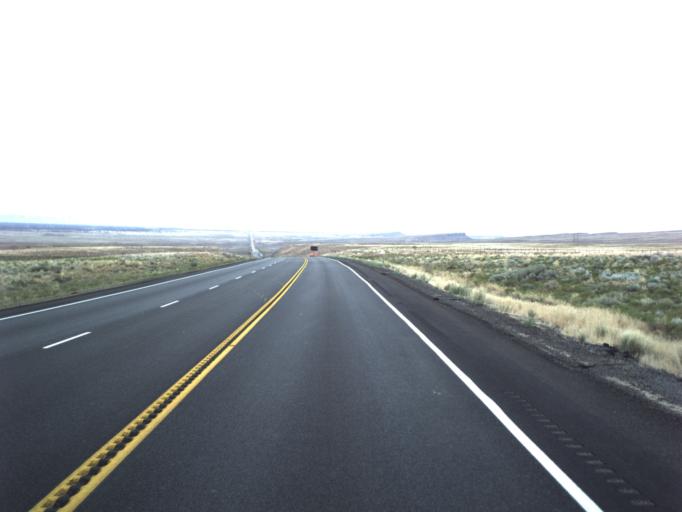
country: US
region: Utah
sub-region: Carbon County
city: East Carbon City
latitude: 39.4804
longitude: -110.5097
